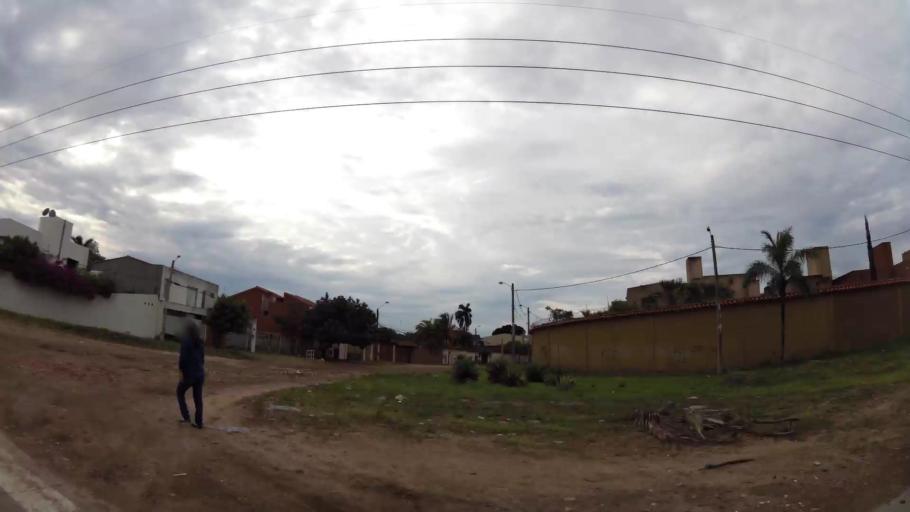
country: BO
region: Santa Cruz
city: Santa Cruz de la Sierra
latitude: -17.7384
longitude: -63.1620
